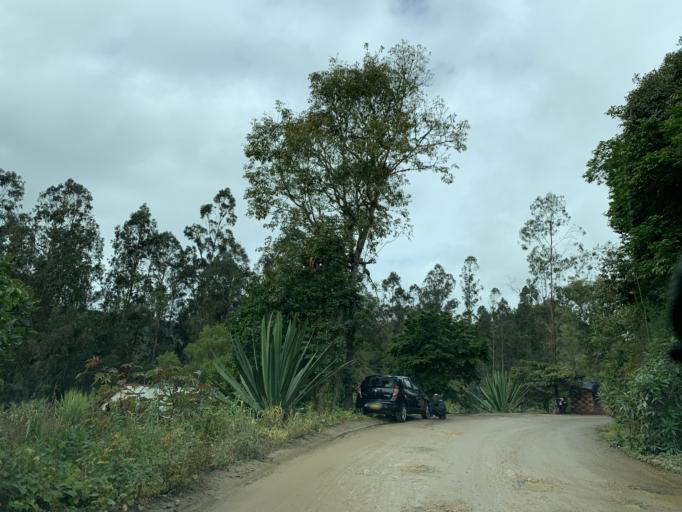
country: CO
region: Boyaca
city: Tibana
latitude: 5.3143
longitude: -73.4228
